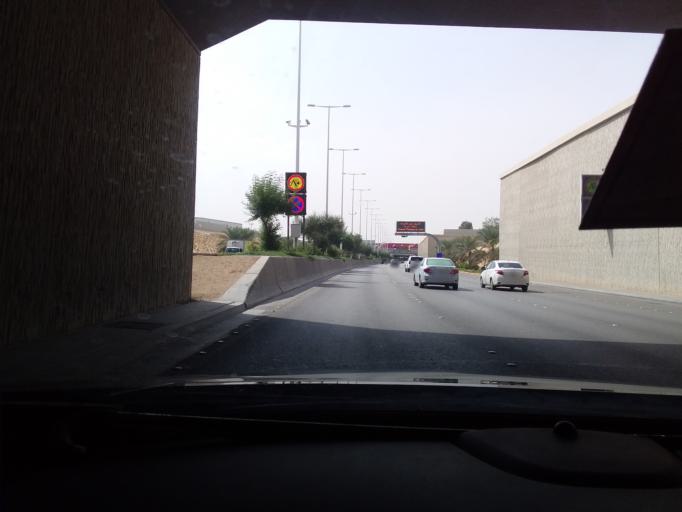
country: SA
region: Ar Riyad
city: Riyadh
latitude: 24.7336
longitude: 46.7366
